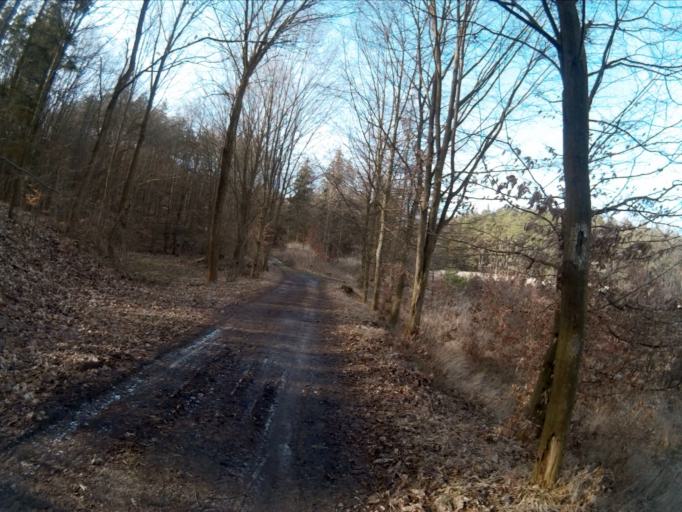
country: CZ
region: Vysocina
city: Mohelno
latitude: 49.1465
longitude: 16.1659
